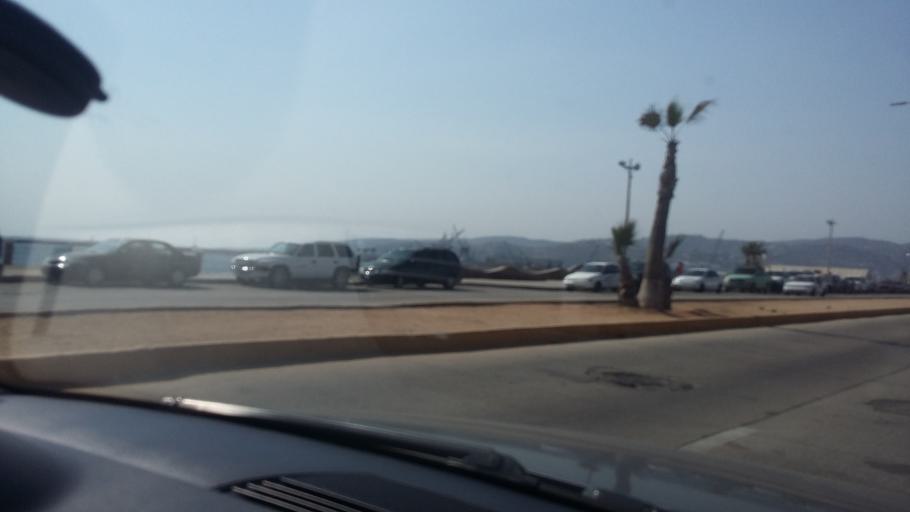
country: MX
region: Baja California
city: Ensenada
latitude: 31.8382
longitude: -116.6104
